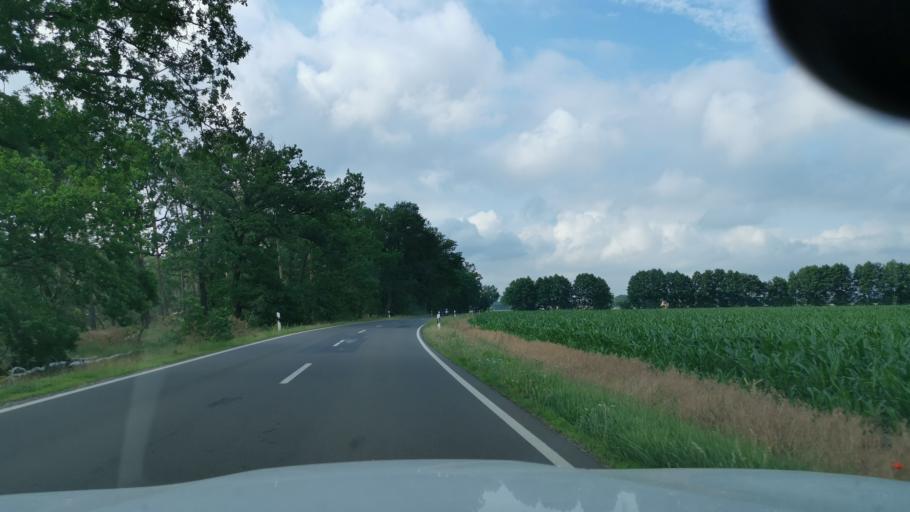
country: DE
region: Saxony-Anhalt
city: Annaburg
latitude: 51.7498
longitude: 13.0432
